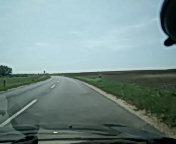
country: HU
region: Fejer
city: Bicske
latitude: 47.4804
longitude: 18.5747
